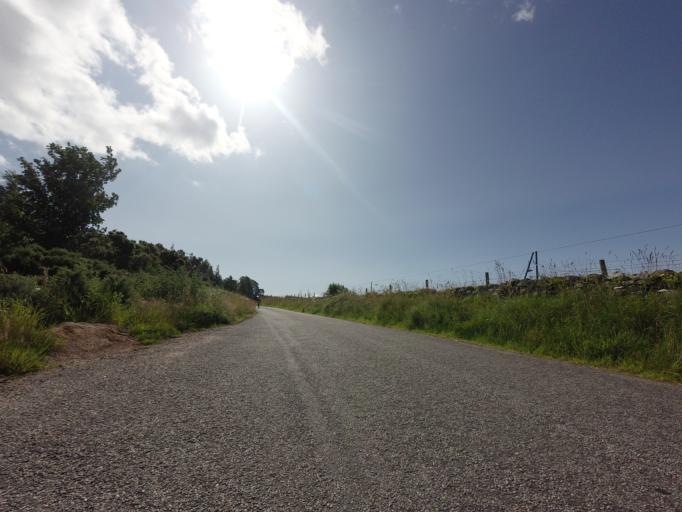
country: GB
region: Scotland
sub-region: Highland
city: Nairn
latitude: 57.5316
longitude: -3.8639
